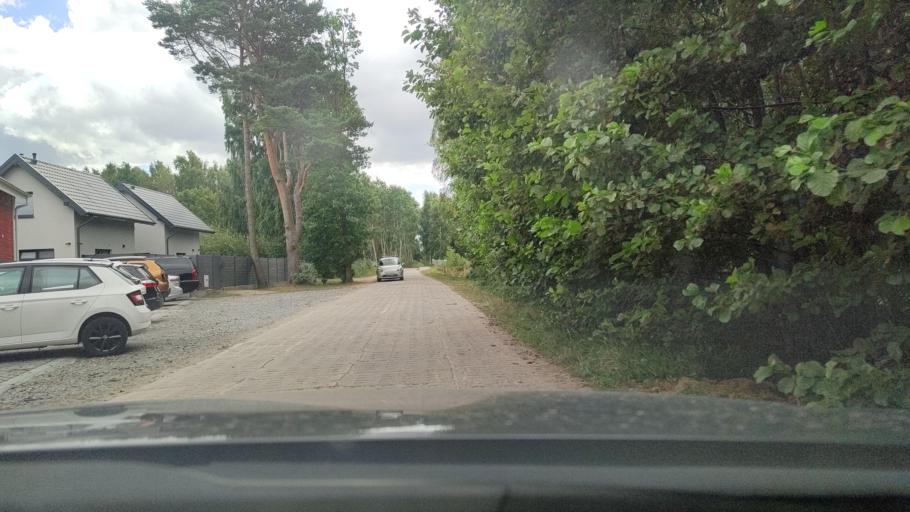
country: PL
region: Pomeranian Voivodeship
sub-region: Powiat pucki
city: Krokowa
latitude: 54.8278
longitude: 18.0930
